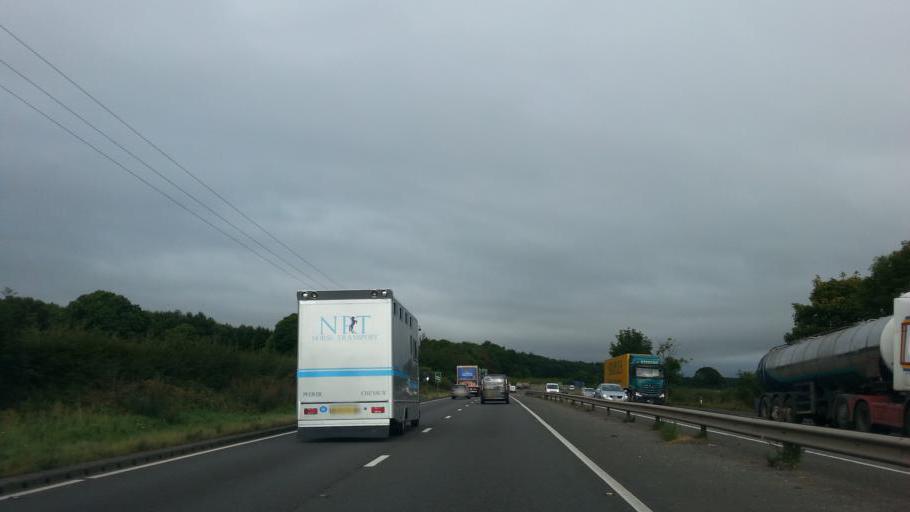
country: GB
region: England
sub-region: Nottinghamshire
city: Babworth
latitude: 53.2898
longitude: -1.0175
